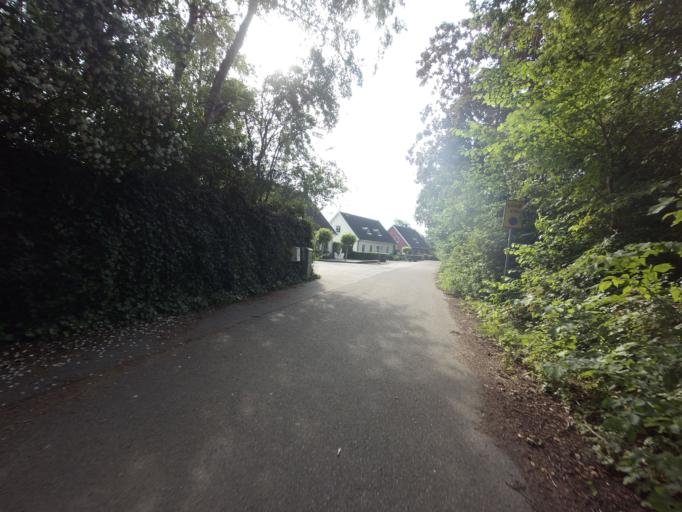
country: SE
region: Skane
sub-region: Malmo
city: Tygelsjo
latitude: 55.4967
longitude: 13.0086
